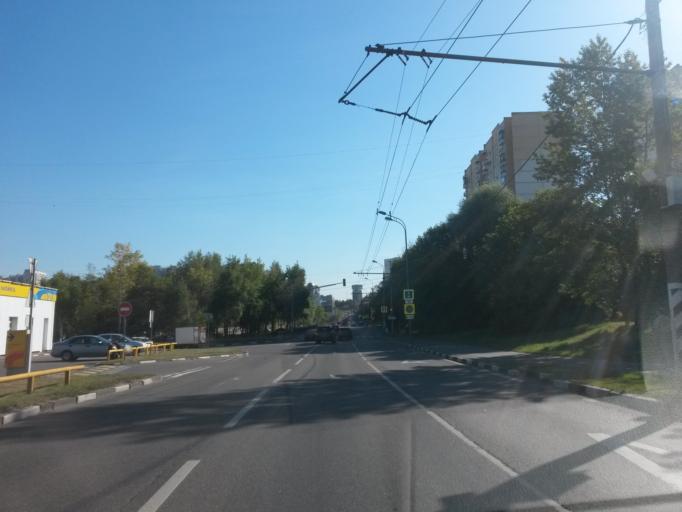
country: RU
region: Moscow
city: Yasenevo
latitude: 55.6201
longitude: 37.5424
